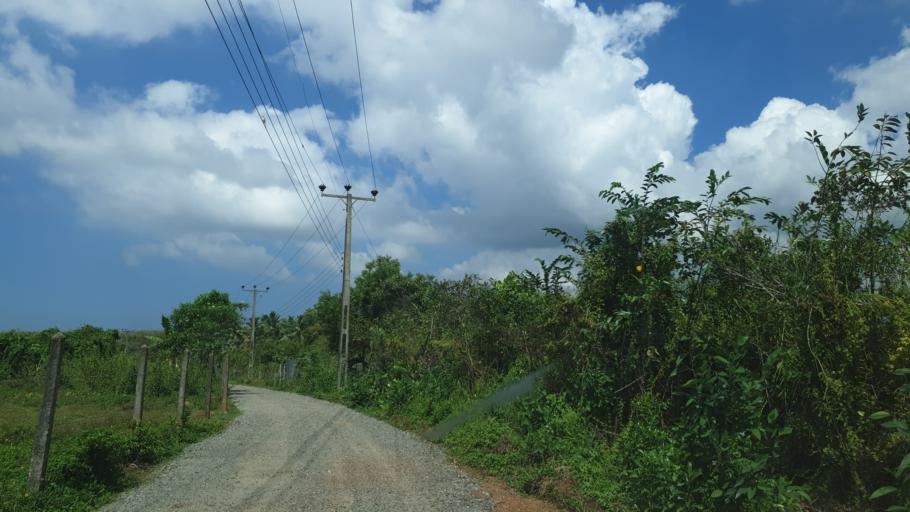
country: LK
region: Western
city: Panadura
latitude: 6.6766
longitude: 79.9626
